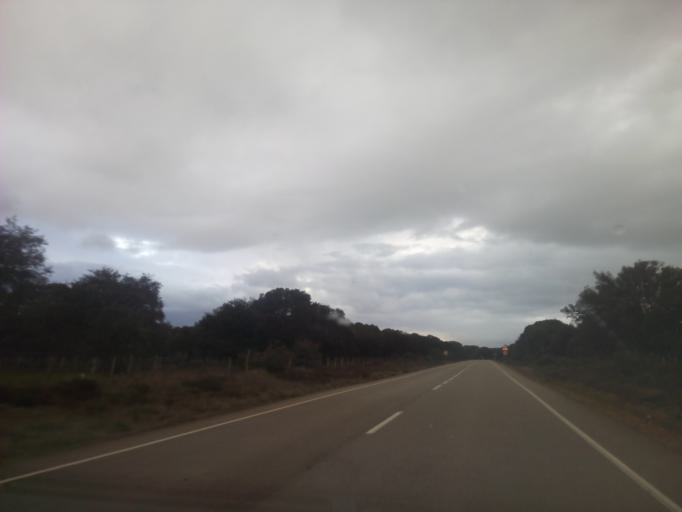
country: ES
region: Castille and Leon
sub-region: Provincia de Salamanca
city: Abusejo
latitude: 40.6809
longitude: -6.1293
